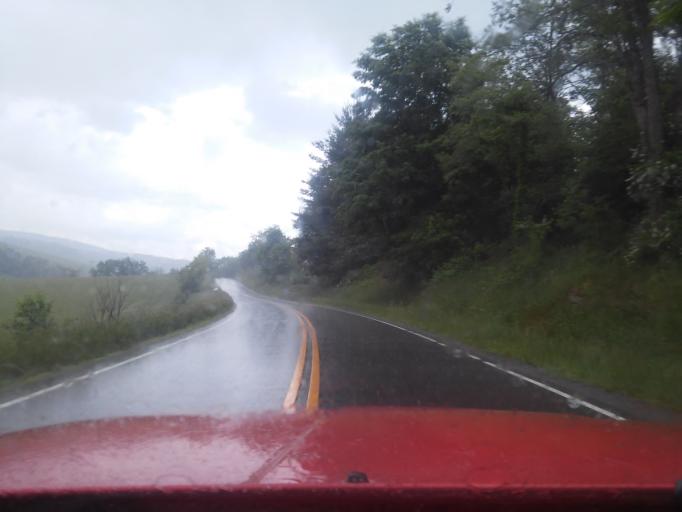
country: US
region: Virginia
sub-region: Montgomery County
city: Blacksburg
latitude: 37.4018
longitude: -80.3099
